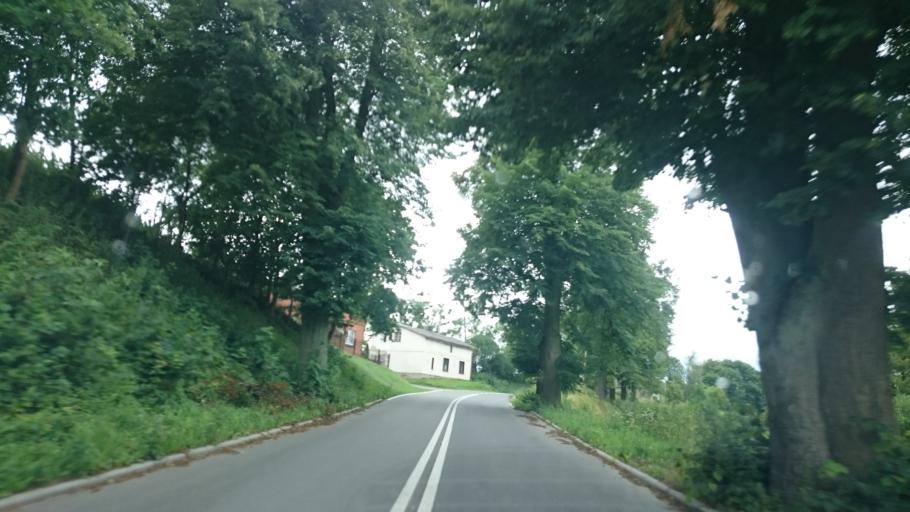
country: PL
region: Kujawsko-Pomorskie
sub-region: Powiat brodnicki
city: Jablonowo Pomorskie
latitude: 53.3436
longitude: 19.2025
